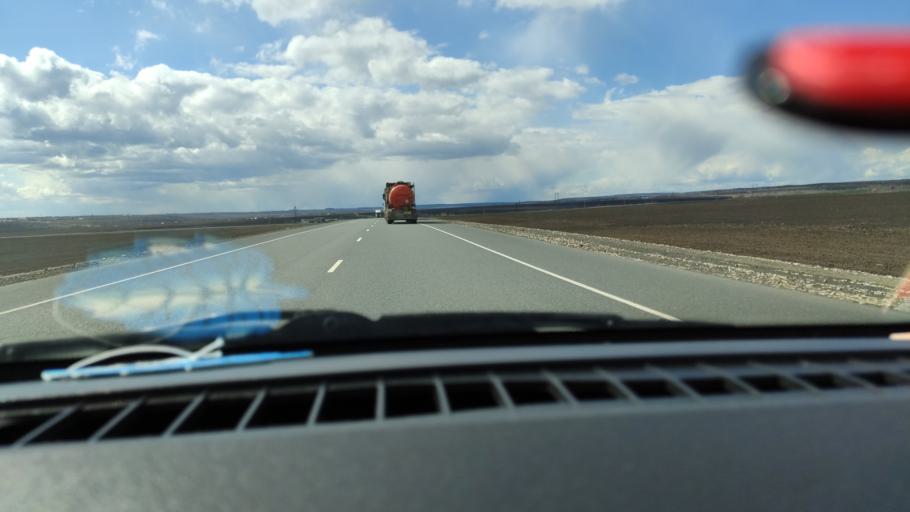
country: RU
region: Samara
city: Varlamovo
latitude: 53.2125
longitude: 48.4218
